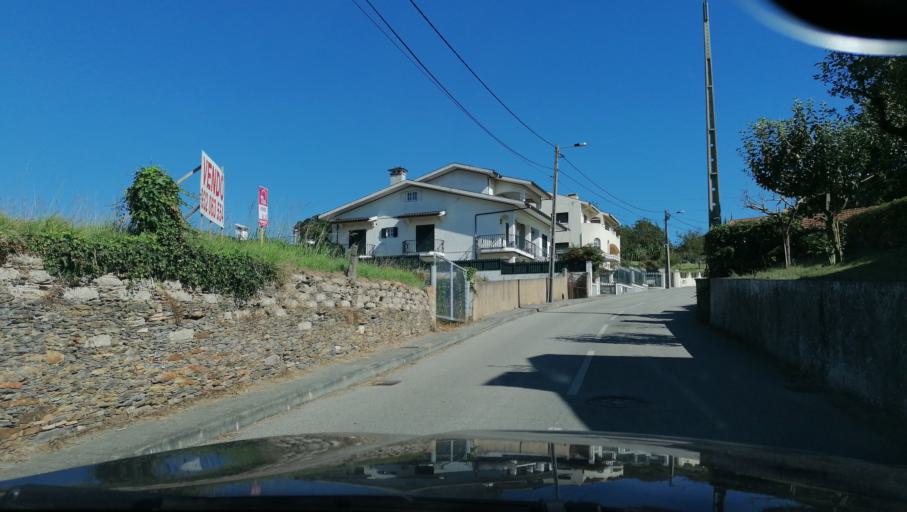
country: PT
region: Aveiro
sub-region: Estarreja
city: Salreu
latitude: 40.7520
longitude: -8.5587
